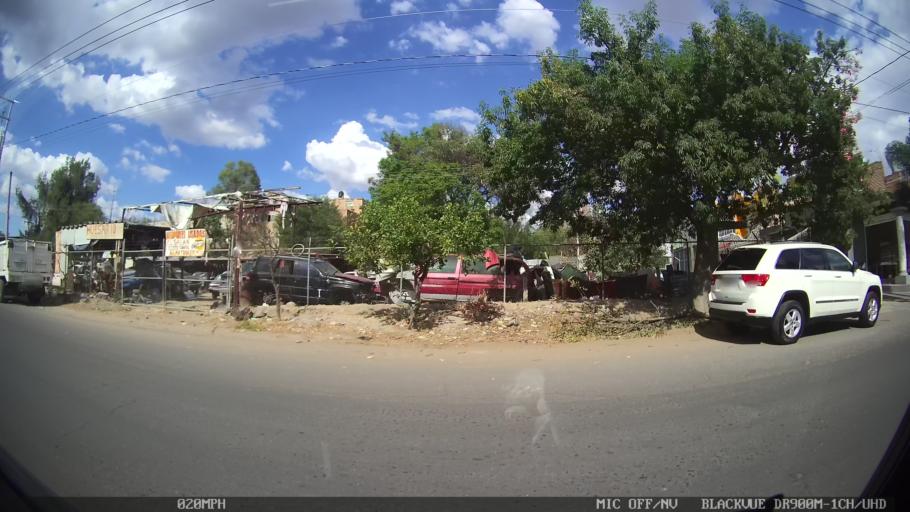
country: MX
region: Jalisco
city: Tlaquepaque
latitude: 20.6633
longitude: -103.2677
